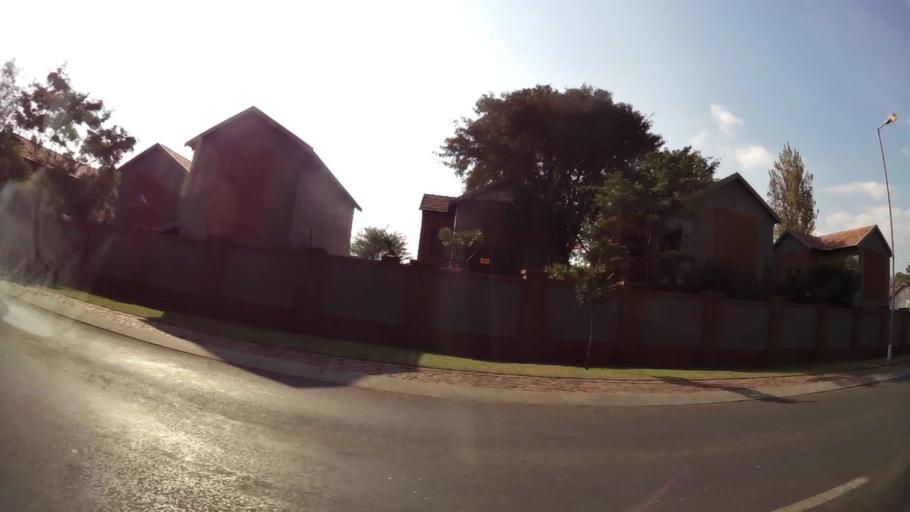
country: ZA
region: Gauteng
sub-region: City of Tshwane Metropolitan Municipality
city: Pretoria
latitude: -25.7709
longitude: 28.3443
